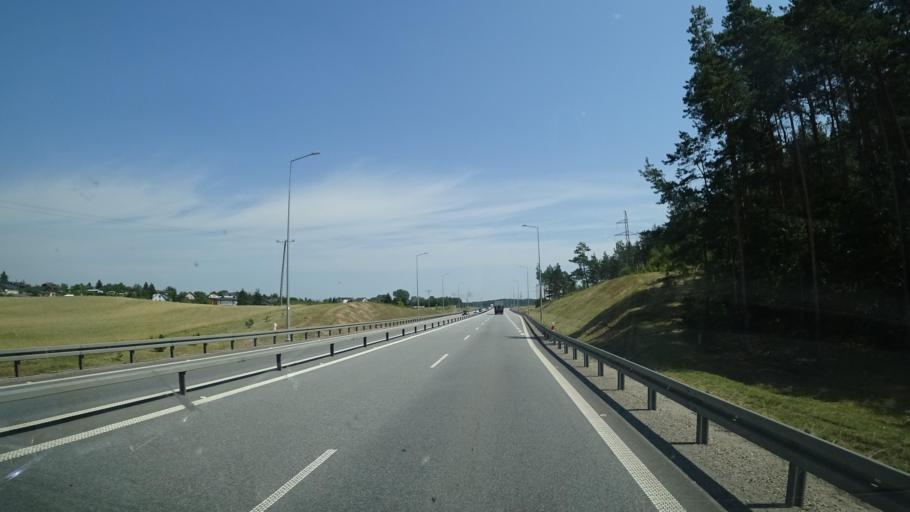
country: PL
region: Pomeranian Voivodeship
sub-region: Powiat koscierski
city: Koscierzyna
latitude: 54.1095
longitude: 17.9876
